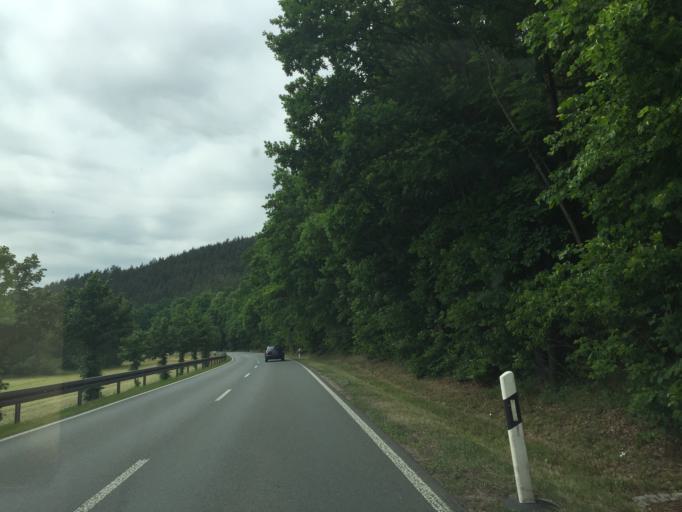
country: DE
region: Thuringia
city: Rottenbach
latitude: 50.6909
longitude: 11.1882
